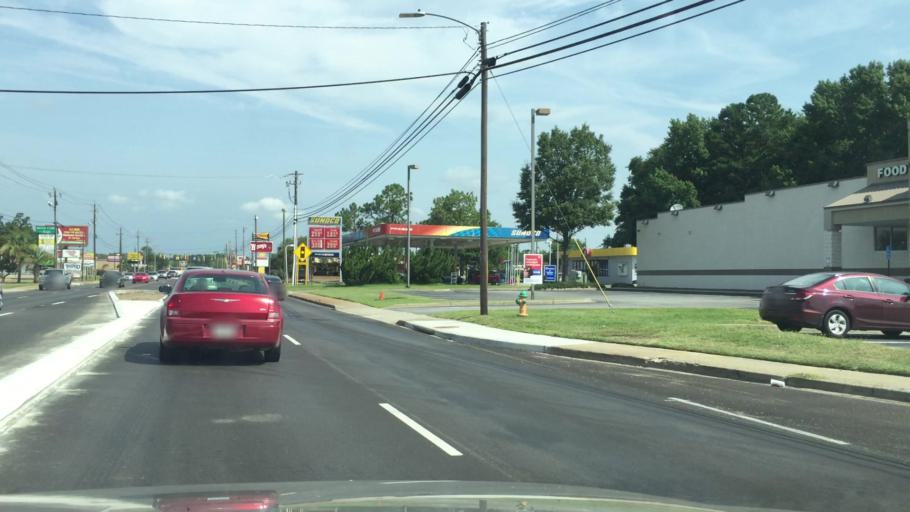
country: US
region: South Carolina
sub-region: Sumter County
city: Sumter
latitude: 33.9498
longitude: -80.3759
